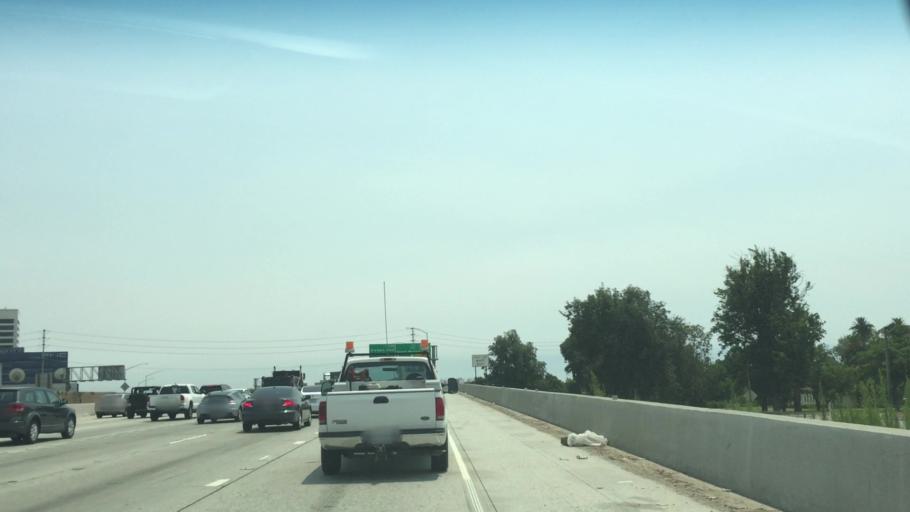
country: US
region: California
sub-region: Los Angeles County
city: Westwood, Los Angeles
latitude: 34.0514
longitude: -118.4496
